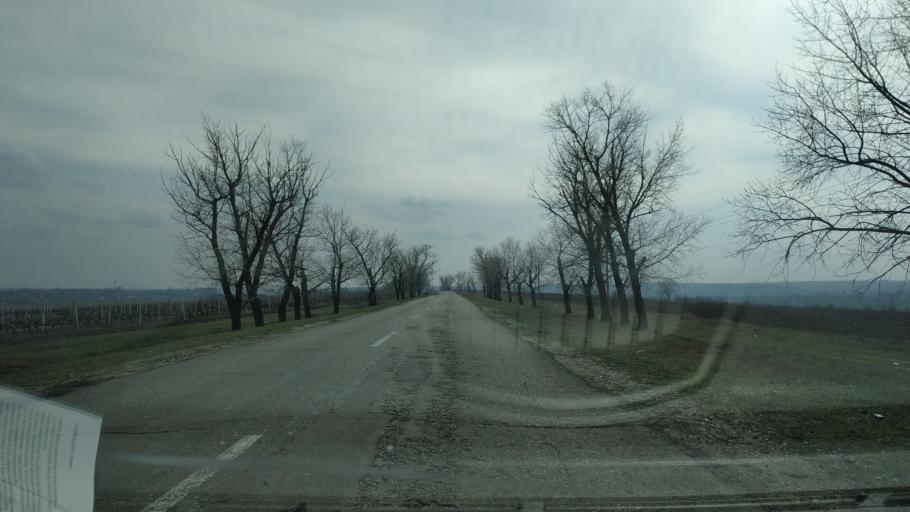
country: MD
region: Gagauzia
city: Vulcanesti
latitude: 45.7073
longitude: 28.4008
